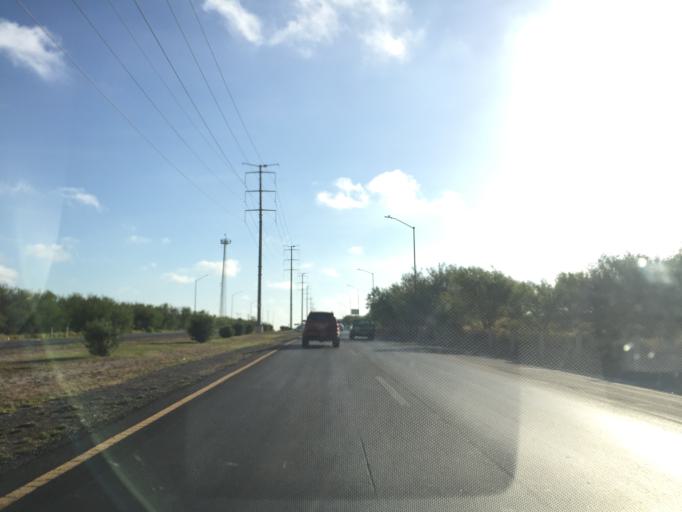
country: MX
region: Tamaulipas
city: Nuevo Laredo
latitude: 27.4316
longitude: -99.5040
